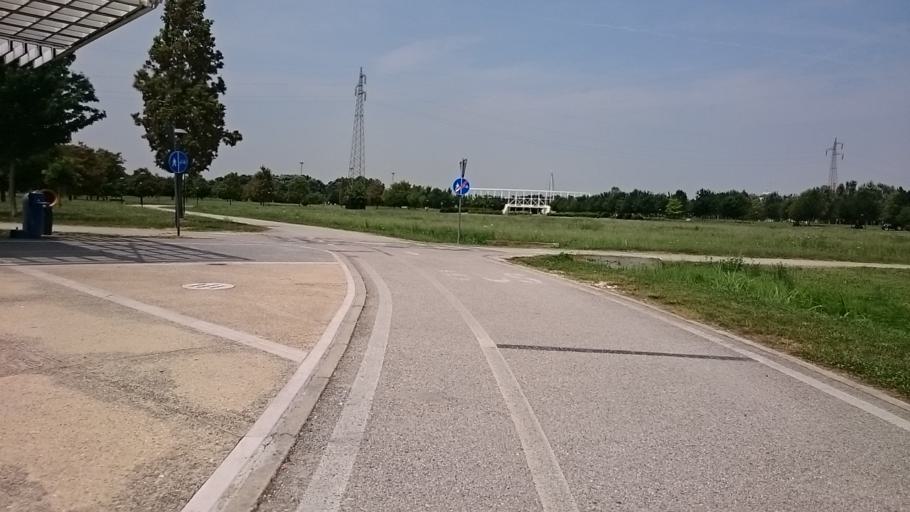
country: IT
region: Veneto
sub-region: Provincia di Venezia
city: Campalto
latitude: 45.4746
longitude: 12.2728
